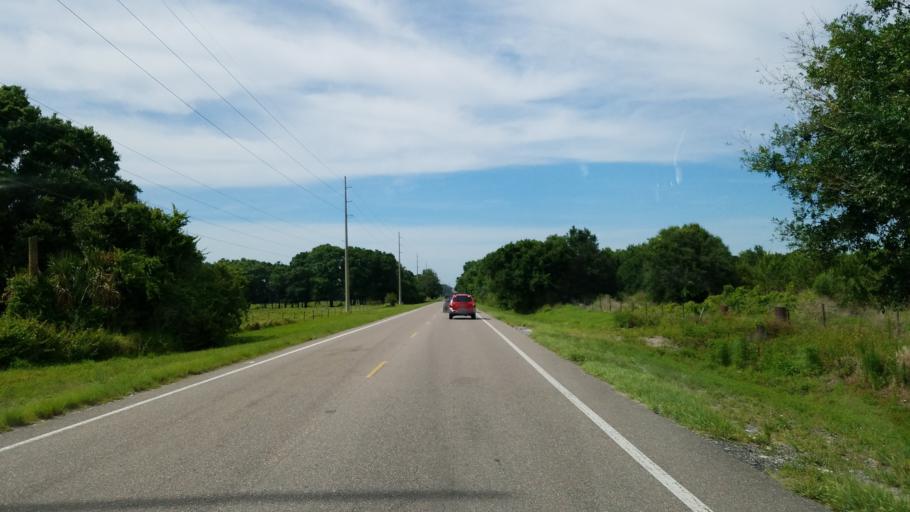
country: US
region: Florida
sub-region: Hillsborough County
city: Balm
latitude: 27.6767
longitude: -82.1462
